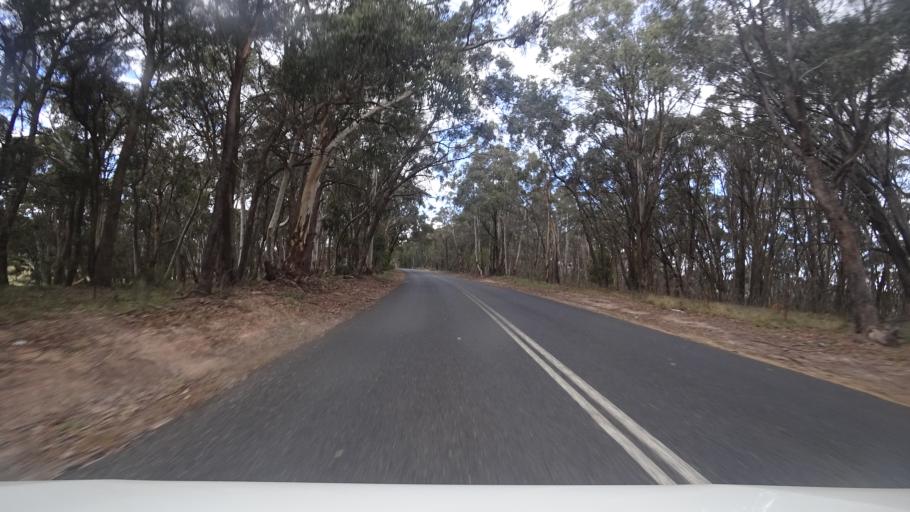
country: AU
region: New South Wales
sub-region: Oberon
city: Oberon
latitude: -33.6505
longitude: 149.8941
